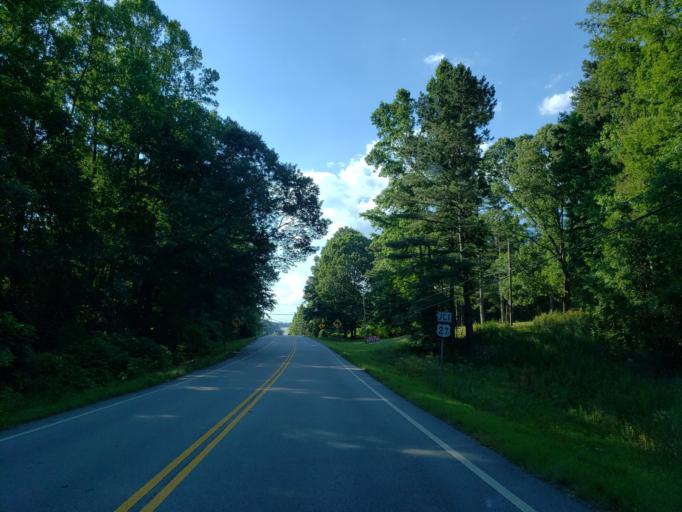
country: US
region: Georgia
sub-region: Haralson County
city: Bremen
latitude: 33.7500
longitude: -85.1570
